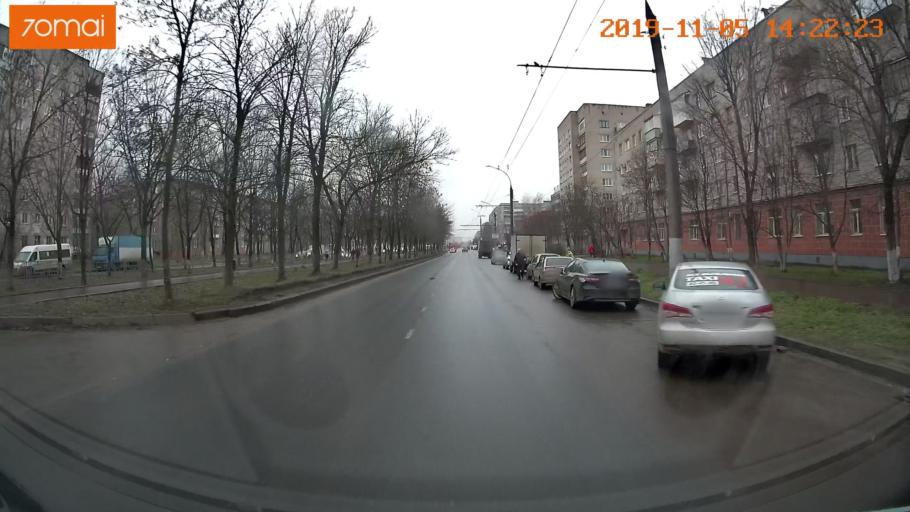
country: RU
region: Ivanovo
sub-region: Gorod Ivanovo
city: Ivanovo
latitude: 56.9634
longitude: 41.0047
